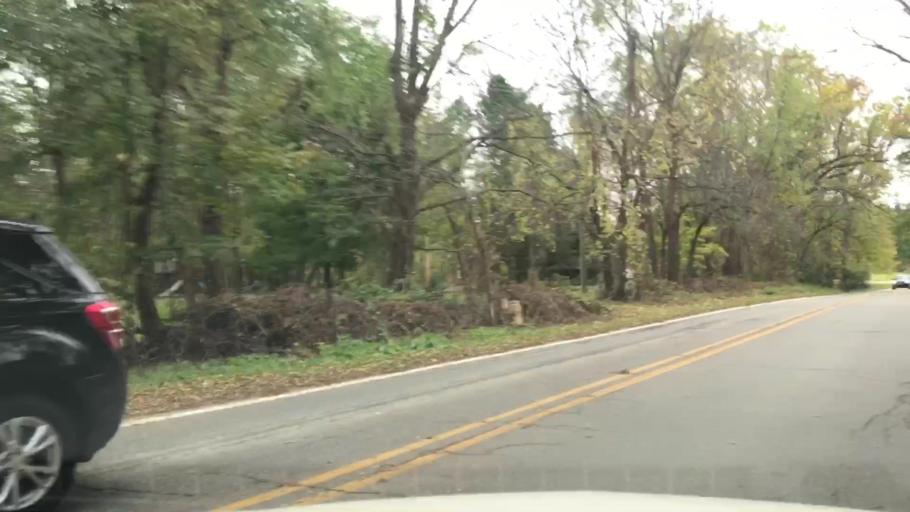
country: US
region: Michigan
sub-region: Macomb County
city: Romeo
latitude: 42.7422
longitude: -83.0569
